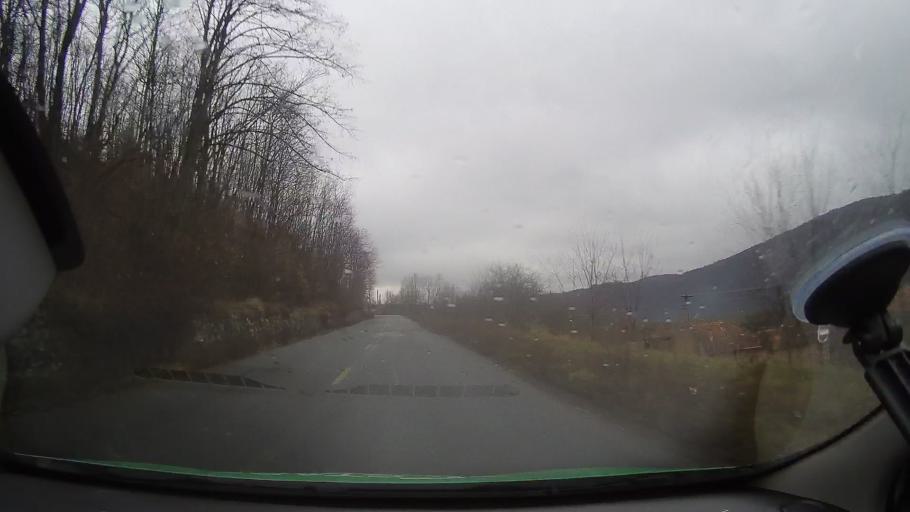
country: RO
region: Arad
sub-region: Comuna Halmagiu
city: Halmagiu
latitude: 46.2365
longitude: 22.5578
